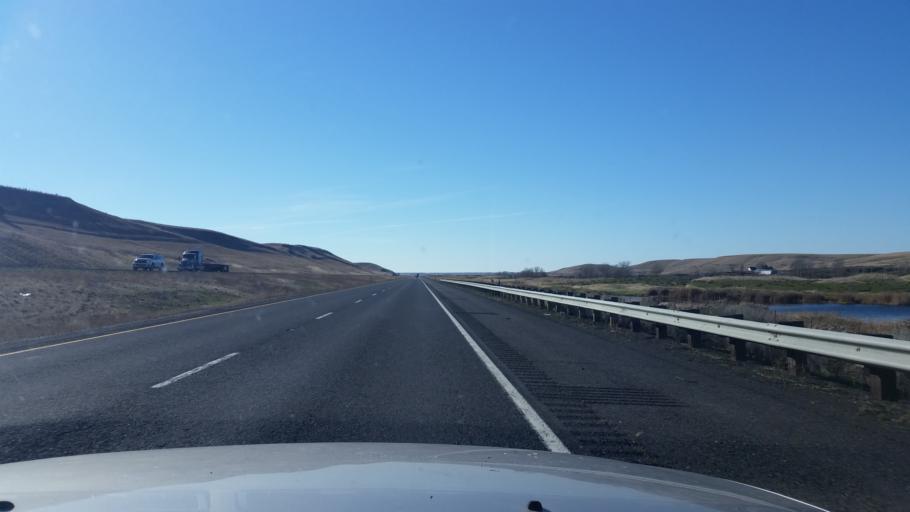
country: US
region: Washington
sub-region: Spokane County
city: Medical Lake
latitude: 47.3624
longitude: -117.8876
